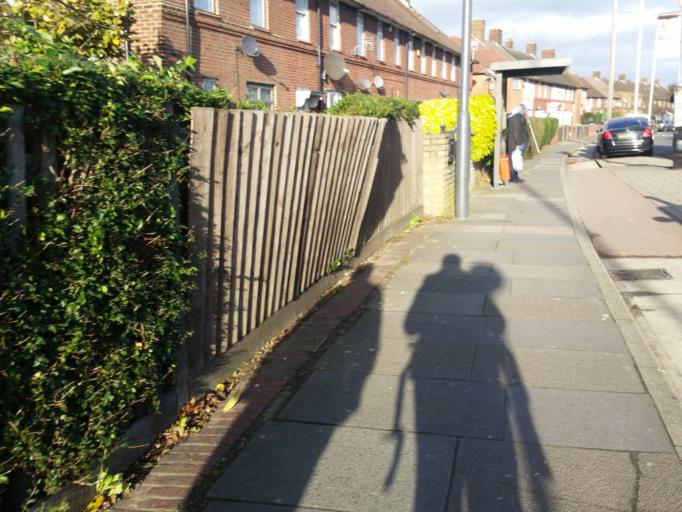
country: GB
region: England
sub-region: Greater London
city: Harringay
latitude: 51.6016
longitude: -0.0913
